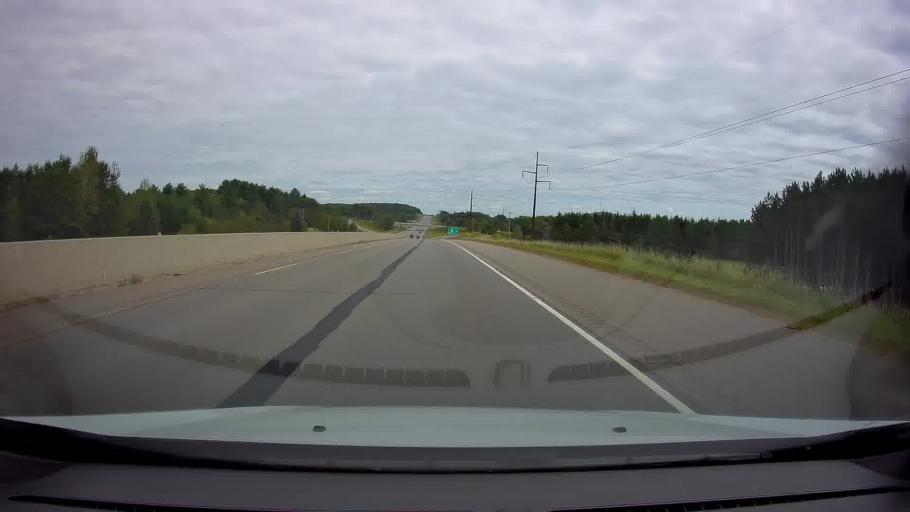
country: US
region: Wisconsin
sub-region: Marathon County
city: Marathon
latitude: 44.9444
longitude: -89.7940
